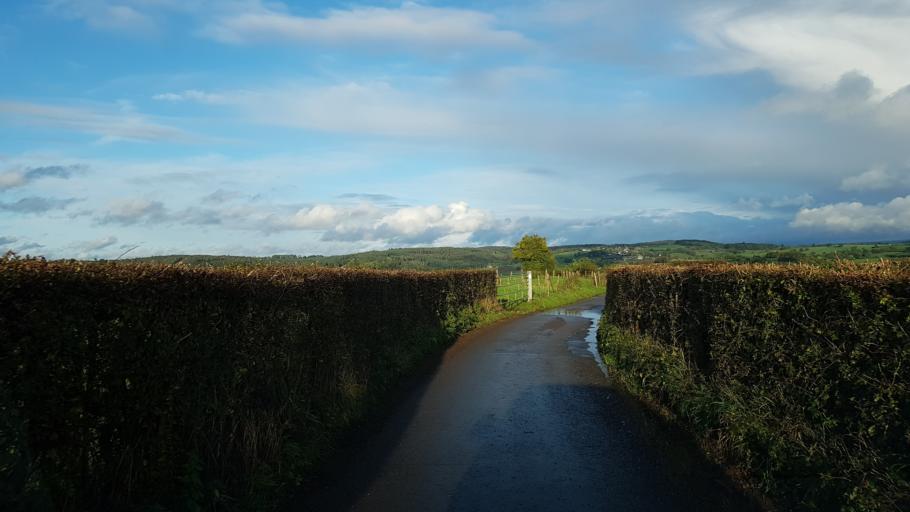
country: BE
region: Wallonia
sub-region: Province de Liege
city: Theux
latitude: 50.5389
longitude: 5.7907
